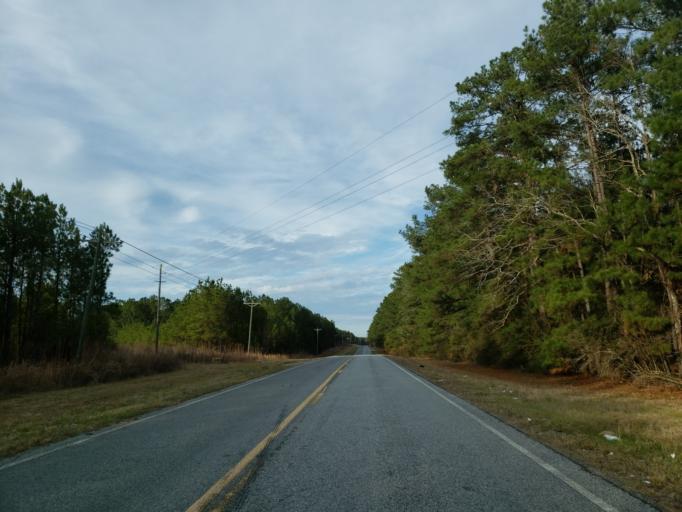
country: US
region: Mississippi
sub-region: Wayne County
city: Waynesboro
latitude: 31.8266
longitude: -88.6905
